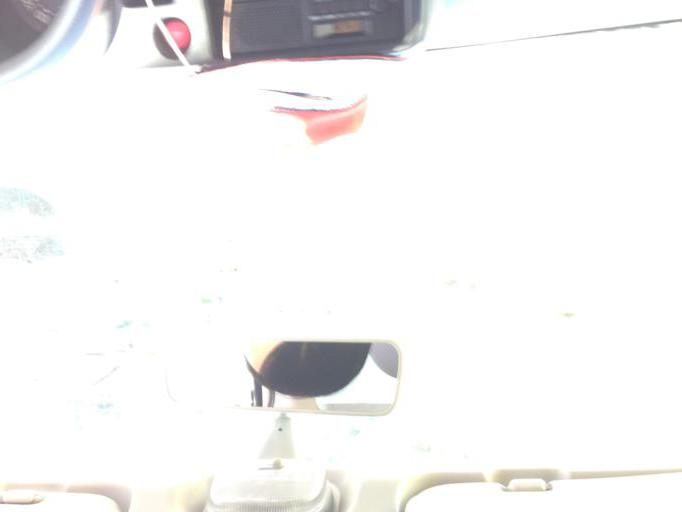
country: JP
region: Gifu
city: Mitake
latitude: 35.6124
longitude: 137.1839
